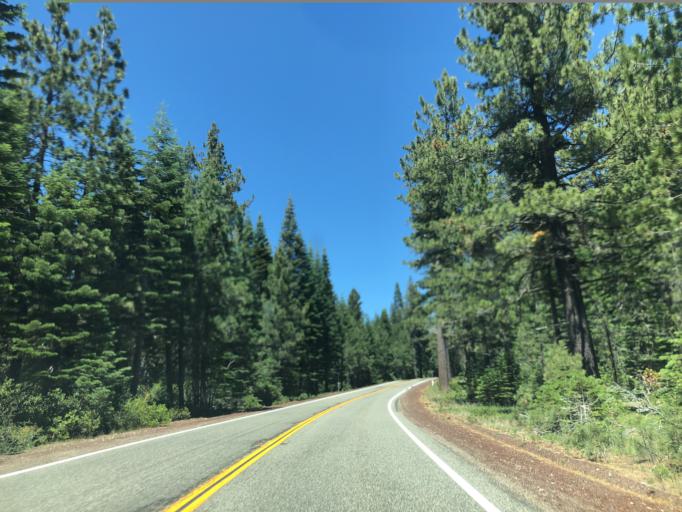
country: US
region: California
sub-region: Shasta County
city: Shingletown
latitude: 40.5539
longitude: -121.5800
